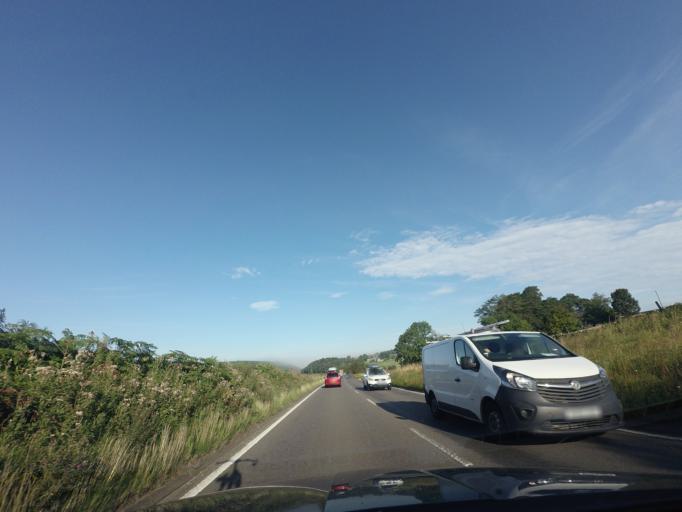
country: GB
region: England
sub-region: Derbyshire
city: Matlock
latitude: 53.2393
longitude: -1.5660
